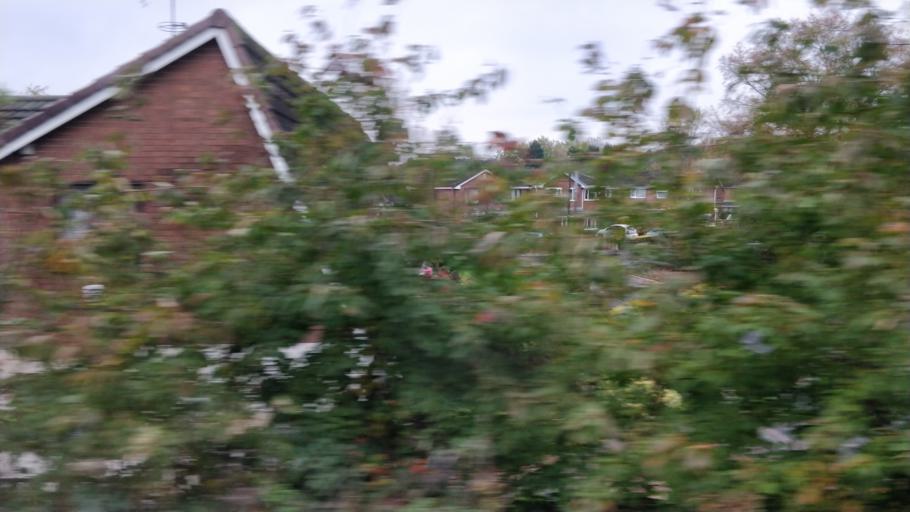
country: GB
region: England
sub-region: Lancashire
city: Parbold
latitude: 53.5918
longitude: -2.7754
